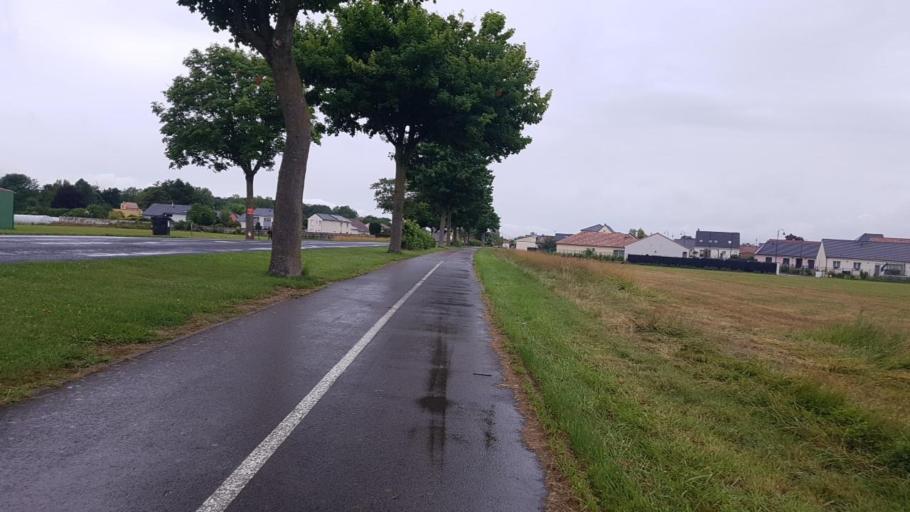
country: FR
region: Champagne-Ardenne
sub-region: Departement de la Marne
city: Sarry
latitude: 48.9129
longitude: 4.4176
